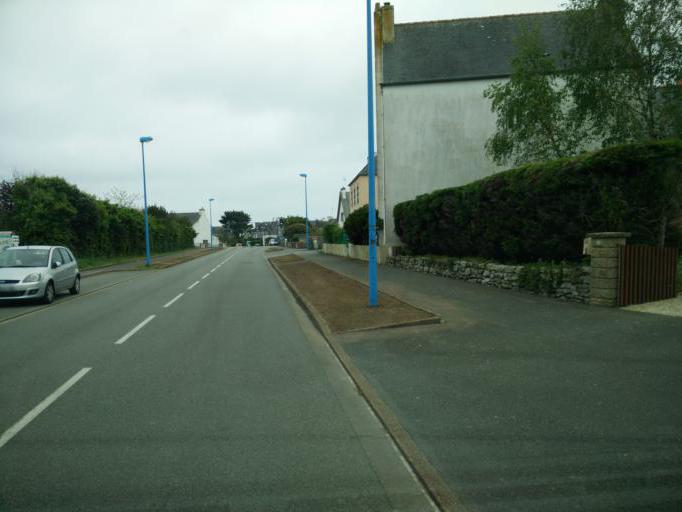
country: FR
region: Brittany
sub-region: Departement du Finistere
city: Plobannalec-Lesconil
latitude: 47.8016
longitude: -4.2215
